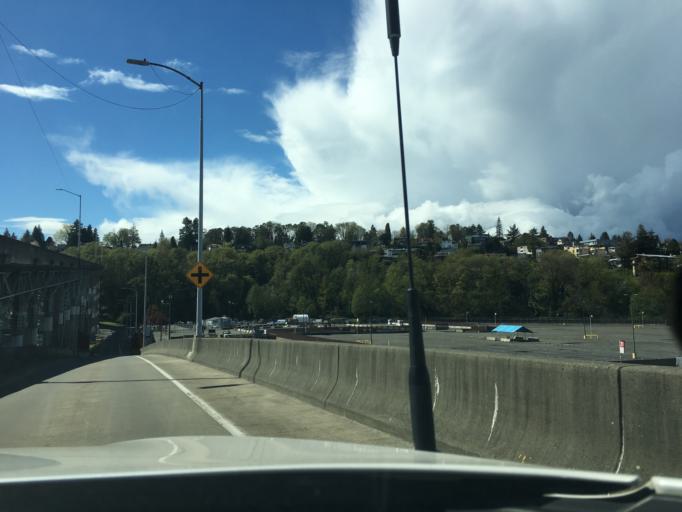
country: US
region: Washington
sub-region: King County
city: Seattle
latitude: 47.6336
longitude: -122.3839
